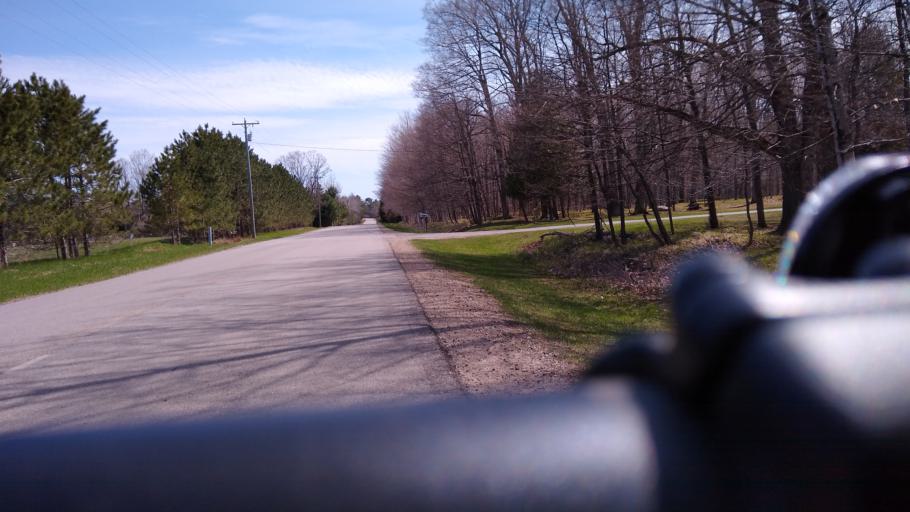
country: US
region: Michigan
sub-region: Delta County
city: Escanaba
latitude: 45.6939
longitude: -87.1526
